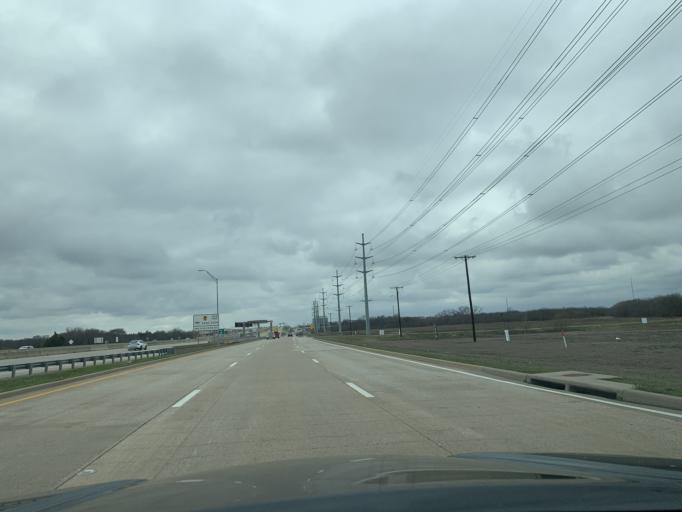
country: US
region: Texas
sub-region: Collin County
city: Fairview
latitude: 33.1498
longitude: -96.6673
